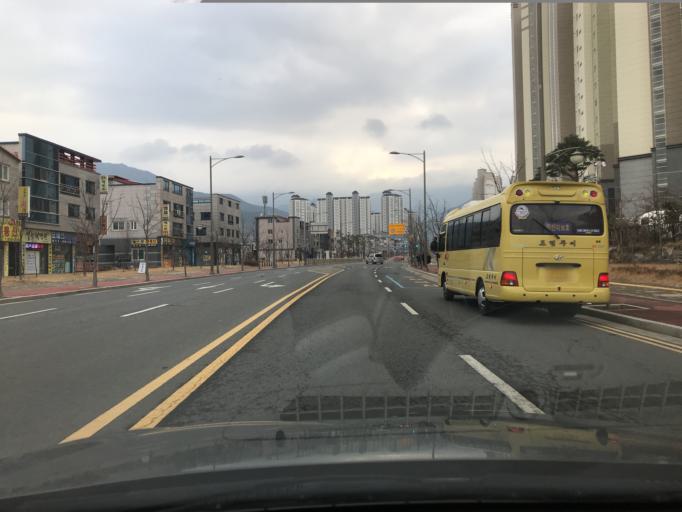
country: KR
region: Daegu
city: Hwawon
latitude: 35.6966
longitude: 128.4551
